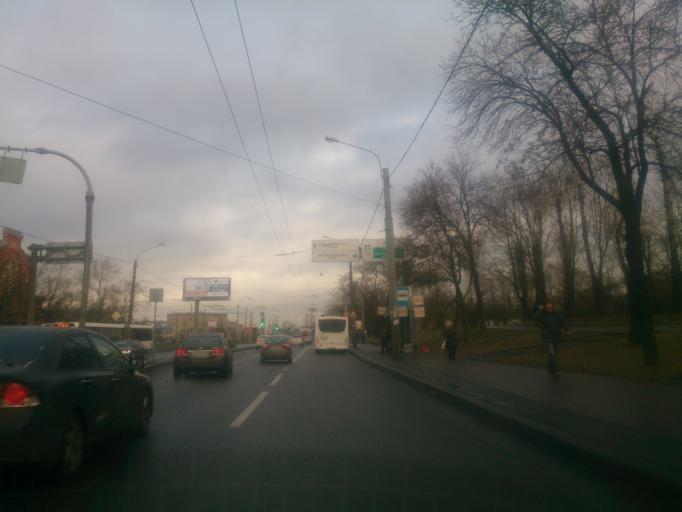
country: RU
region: St.-Petersburg
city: Avtovo
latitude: 59.8590
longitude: 30.2542
